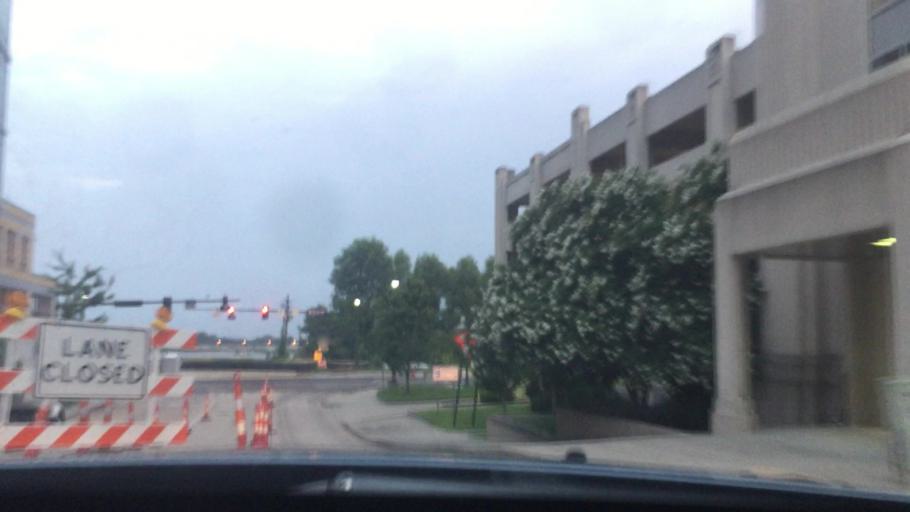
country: US
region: Louisiana
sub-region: West Baton Rouge Parish
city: Port Allen
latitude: 30.4525
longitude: -91.1893
